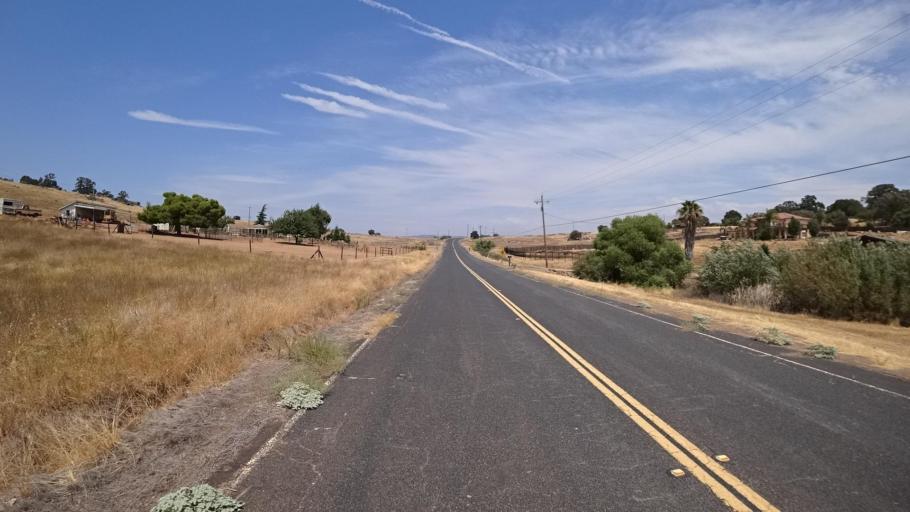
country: US
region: California
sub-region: Tuolumne County
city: Jamestown
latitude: 37.6434
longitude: -120.3312
